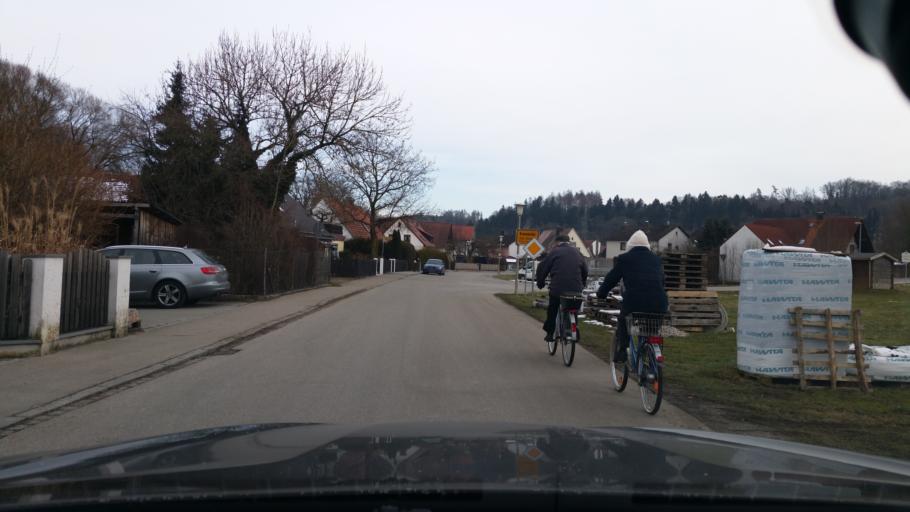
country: DE
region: Bavaria
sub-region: Lower Bavaria
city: Eching
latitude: 48.4980
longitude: 12.0369
